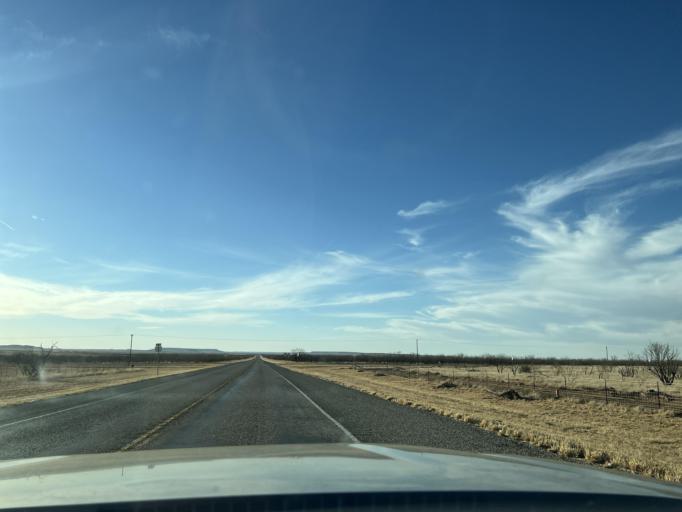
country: US
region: Texas
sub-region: Borden County
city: Gail
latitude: 32.7658
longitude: -101.2880
